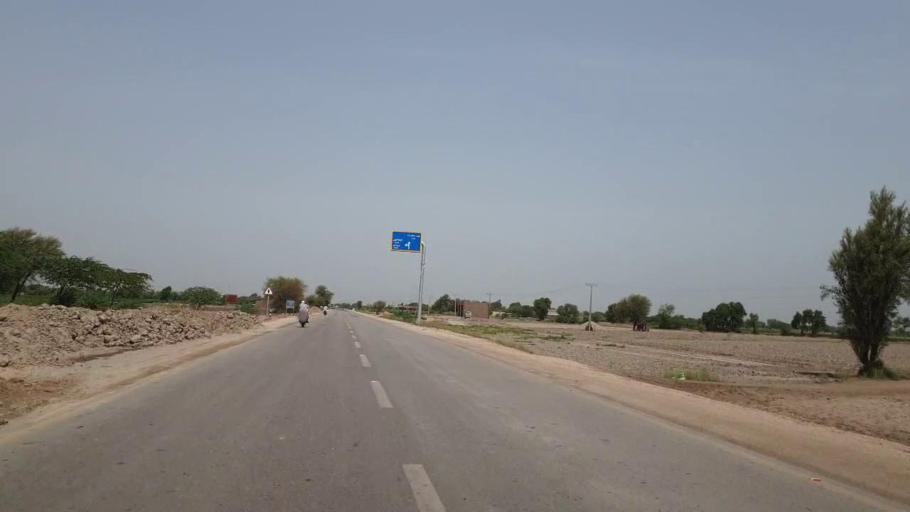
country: PK
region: Sindh
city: Shahpur Chakar
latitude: 26.1899
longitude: 68.5801
